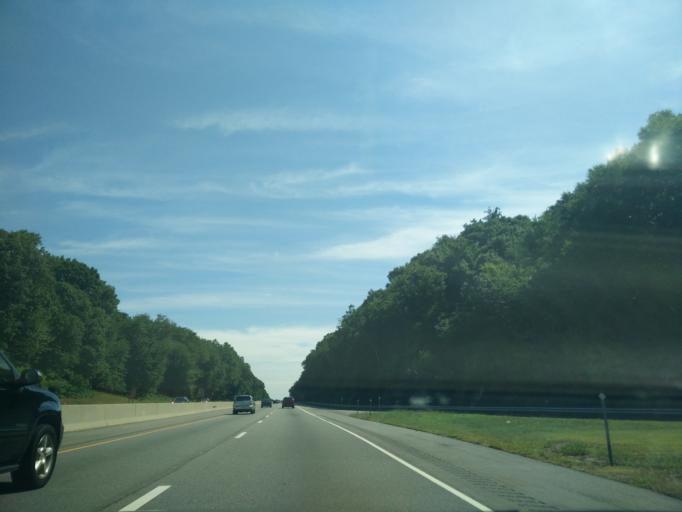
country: US
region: Connecticut
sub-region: New Haven County
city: Madison
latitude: 41.2881
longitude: -72.5986
